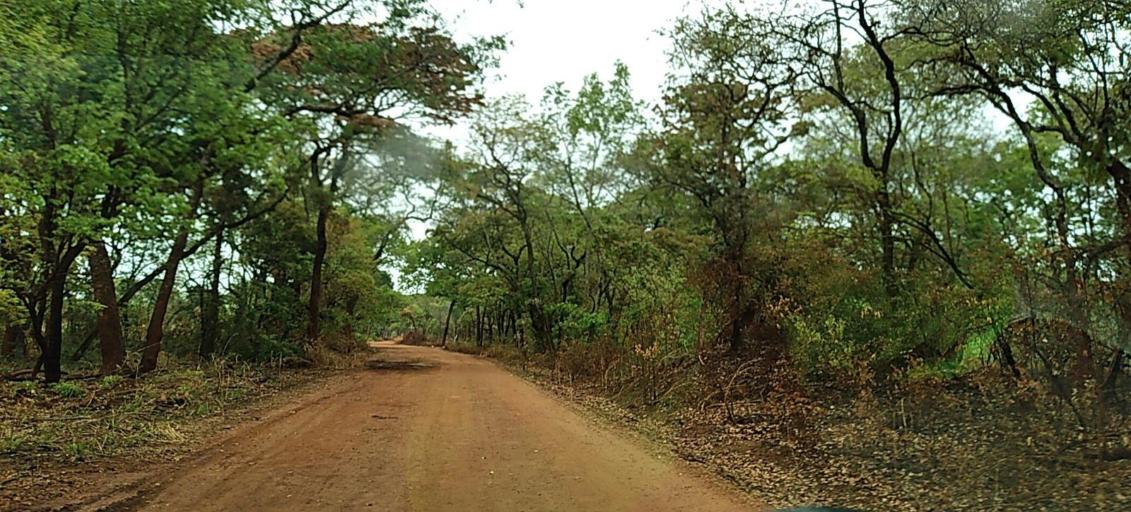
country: ZM
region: North-Western
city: Solwezi
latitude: -12.3103
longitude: 26.5222
